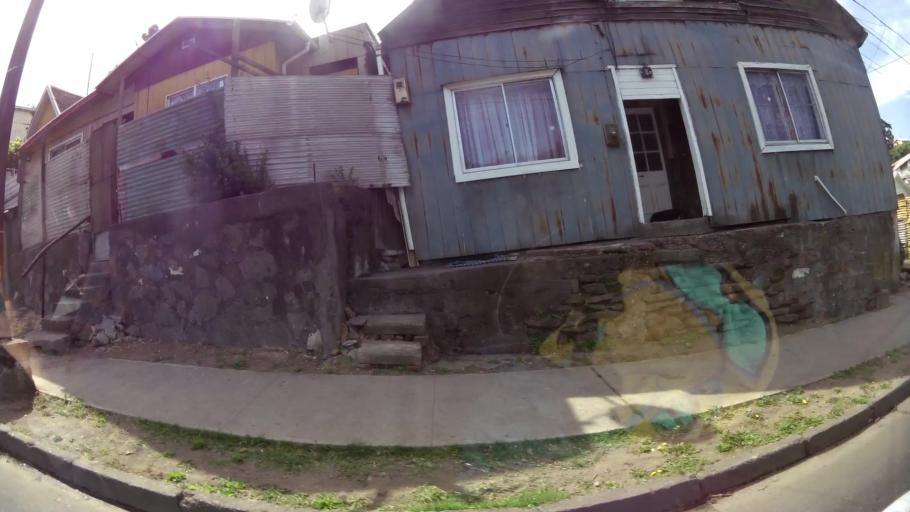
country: CL
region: Biobio
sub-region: Provincia de Concepcion
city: Talcahuano
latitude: -36.7168
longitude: -73.1185
